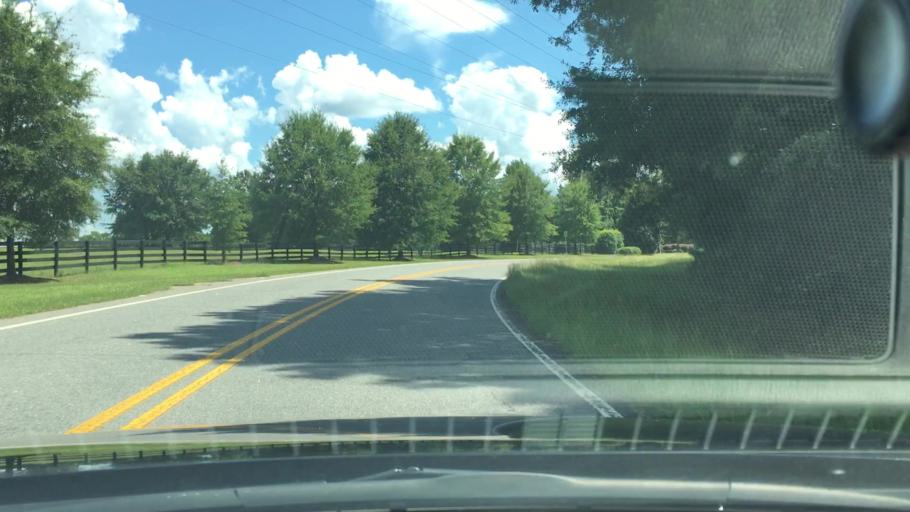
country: US
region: Georgia
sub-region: Putnam County
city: Jefferson
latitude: 33.3774
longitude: -83.2503
